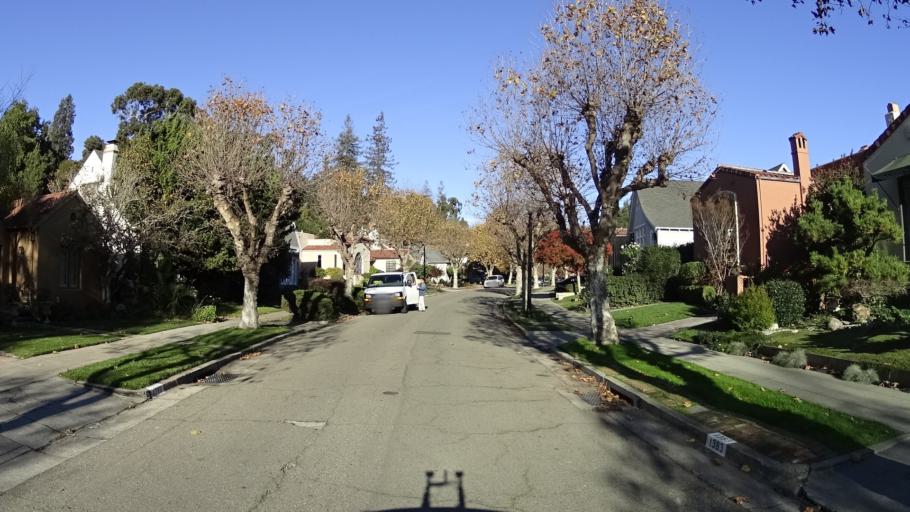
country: US
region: California
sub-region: Alameda County
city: Piedmont
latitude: 37.8084
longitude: -122.2272
